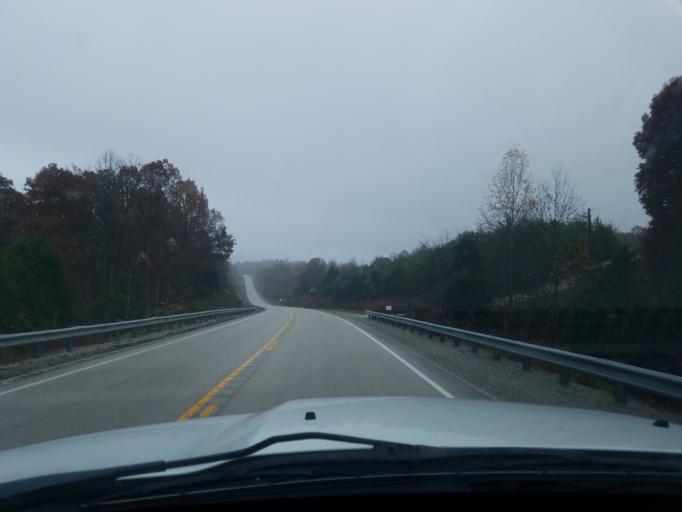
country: US
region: Kentucky
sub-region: Larue County
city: Hodgenville
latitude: 37.4762
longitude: -85.6108
